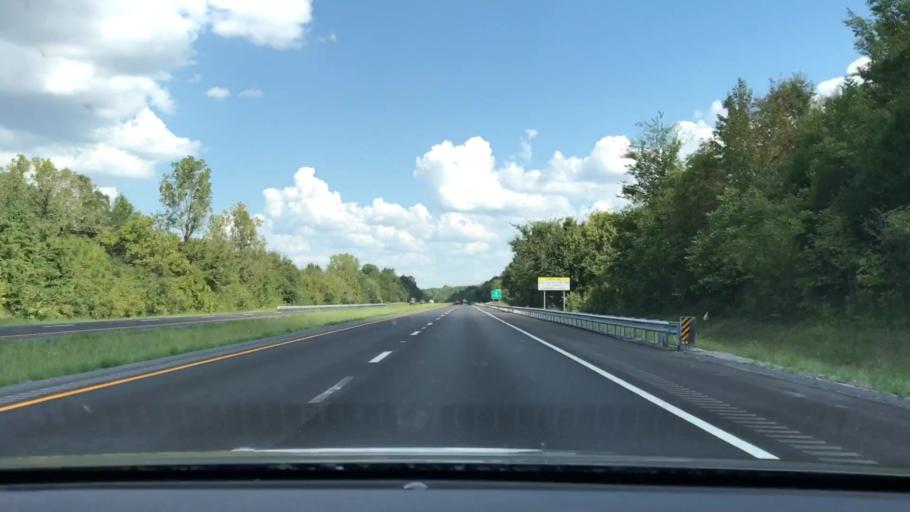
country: US
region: Kentucky
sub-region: Lyon County
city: Eddyville
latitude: 37.0908
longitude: -88.0539
